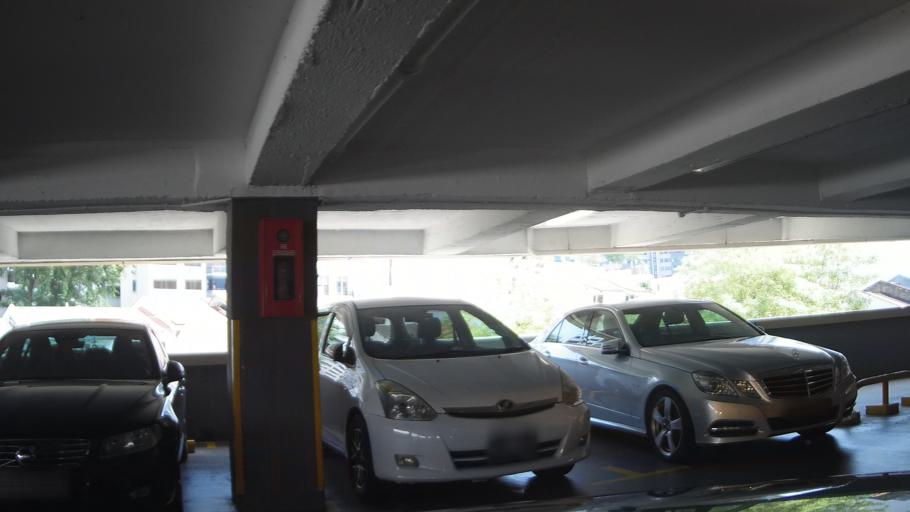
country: SG
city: Singapore
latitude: 1.2854
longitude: 103.8281
